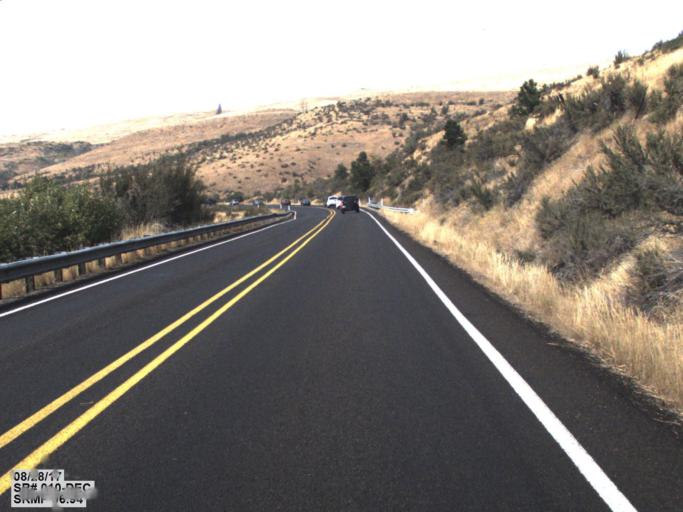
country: US
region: Washington
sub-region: Kittitas County
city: Ellensburg
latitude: 47.1131
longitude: -120.7160
